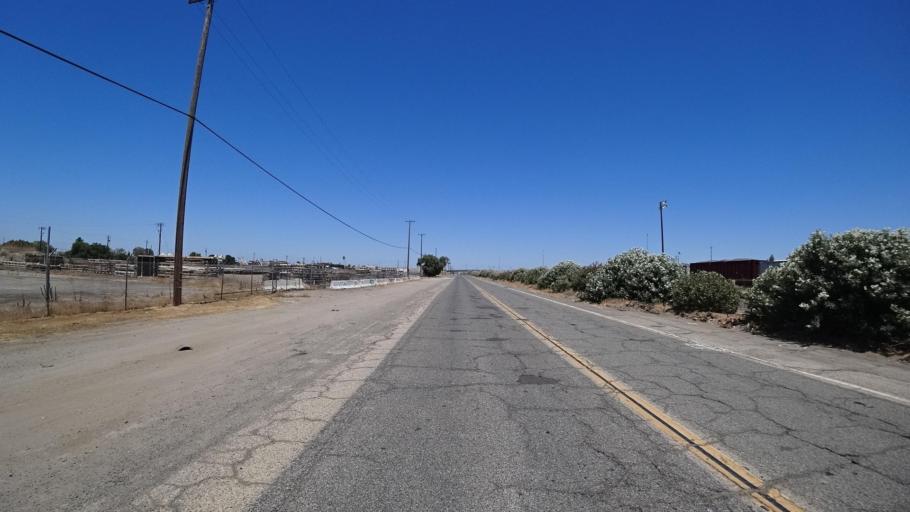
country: US
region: California
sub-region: Fresno County
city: Fresno
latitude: 36.7008
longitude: -119.7594
